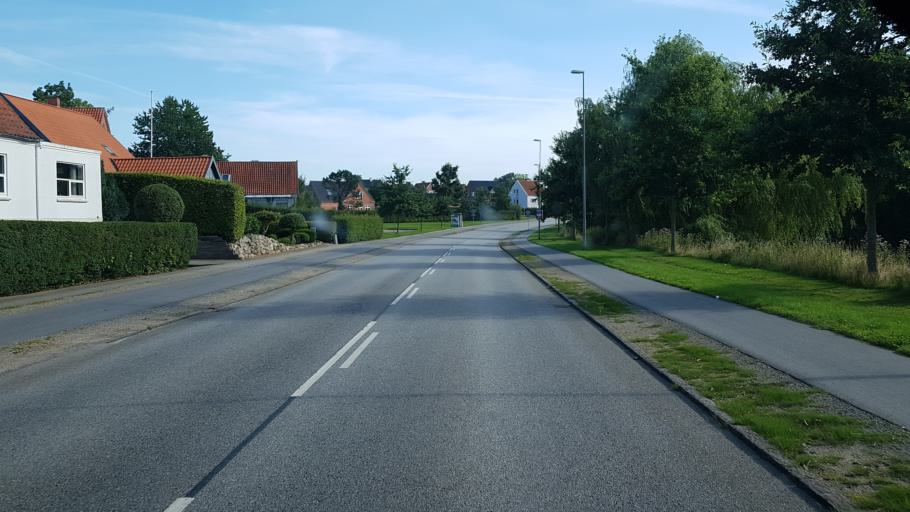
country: DK
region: South Denmark
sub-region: Haderslev Kommune
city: Haderslev
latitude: 55.2393
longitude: 9.4944
